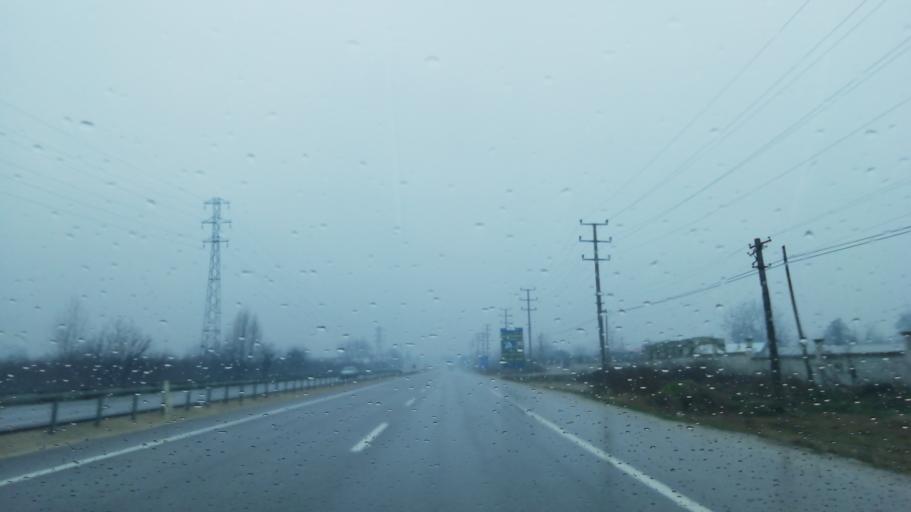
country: TR
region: Sakarya
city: Akyazi
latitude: 40.6388
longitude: 30.6194
